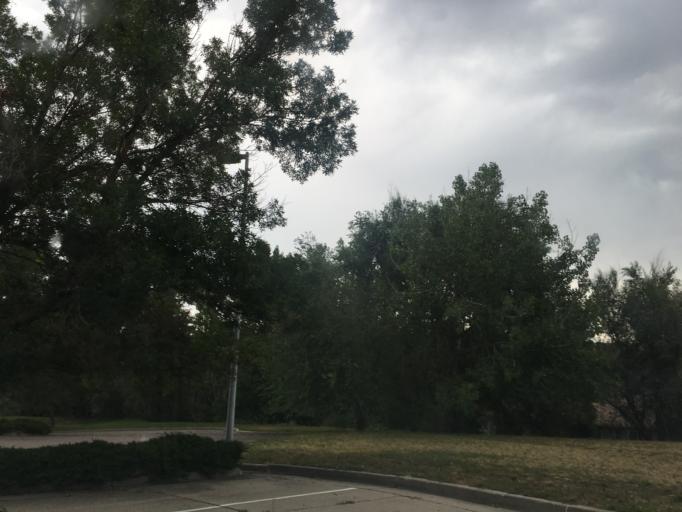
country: US
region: Colorado
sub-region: Arapahoe County
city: Sheridan
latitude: 39.6562
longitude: -105.0337
